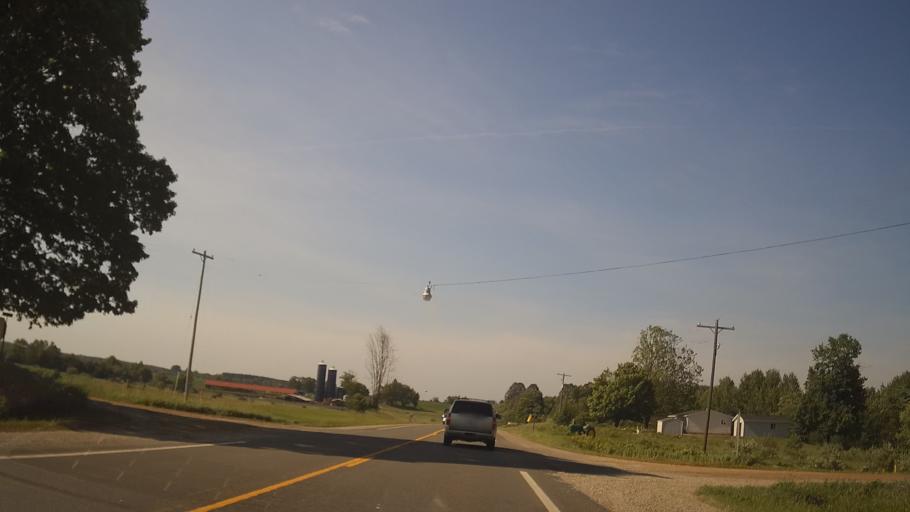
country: US
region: Michigan
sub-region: Ogemaw County
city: West Branch
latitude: 44.3776
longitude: -84.1159
